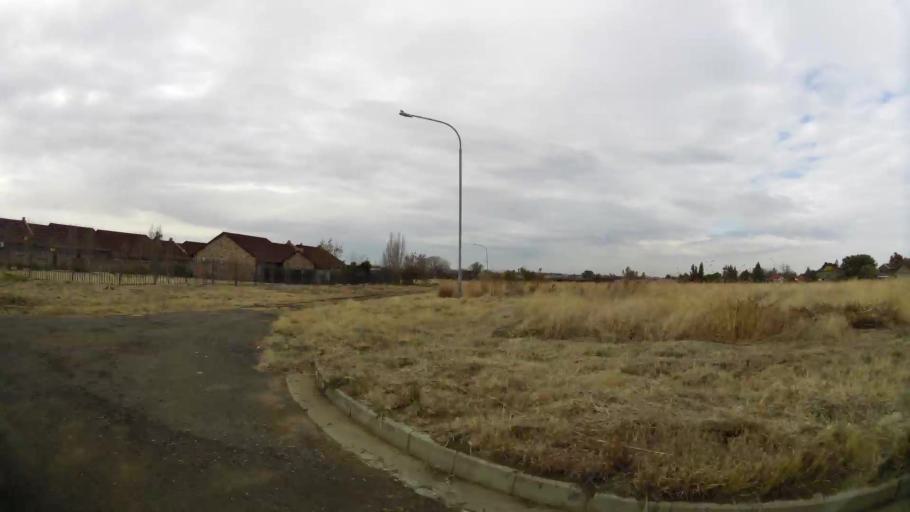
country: ZA
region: Orange Free State
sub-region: Fezile Dabi District Municipality
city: Kroonstad
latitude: -27.6291
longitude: 27.2432
